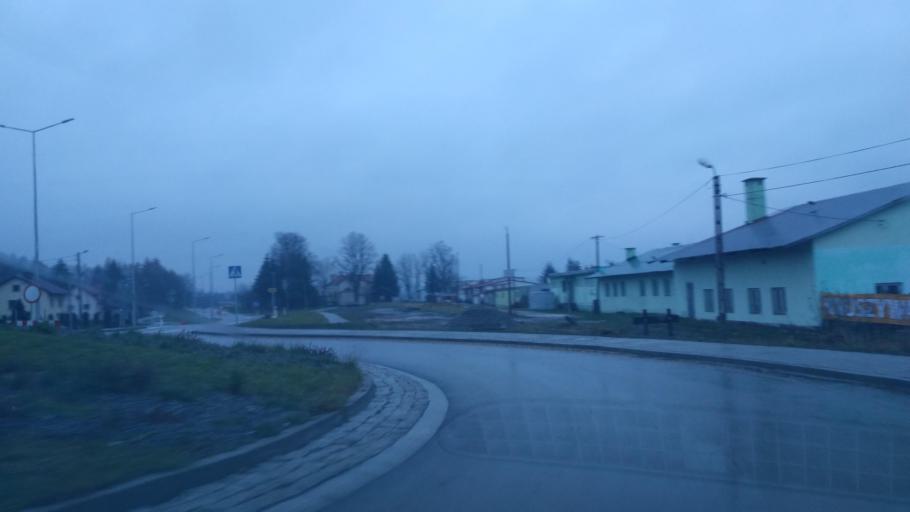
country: PL
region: Subcarpathian Voivodeship
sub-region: Powiat rzeszowski
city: Dynow
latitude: 49.8033
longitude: 22.2398
